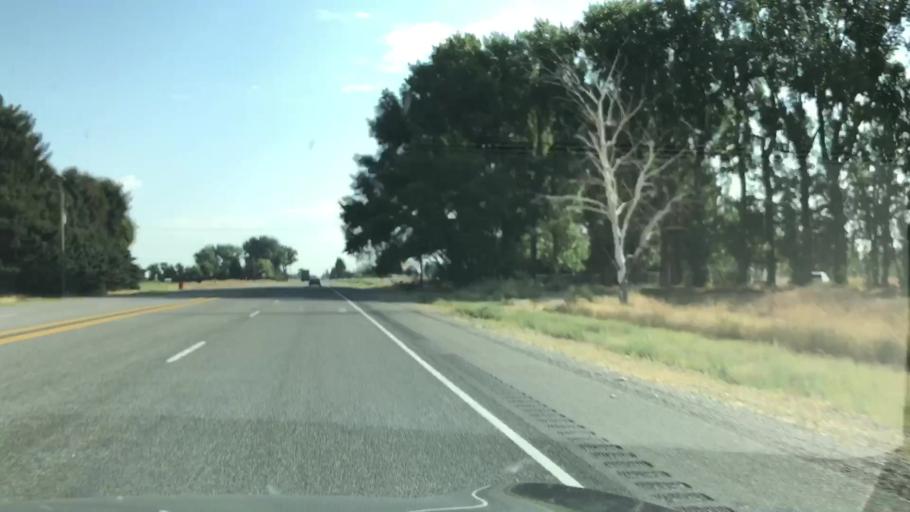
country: US
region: Idaho
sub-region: Bonneville County
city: Iona
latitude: 43.5465
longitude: -111.9551
